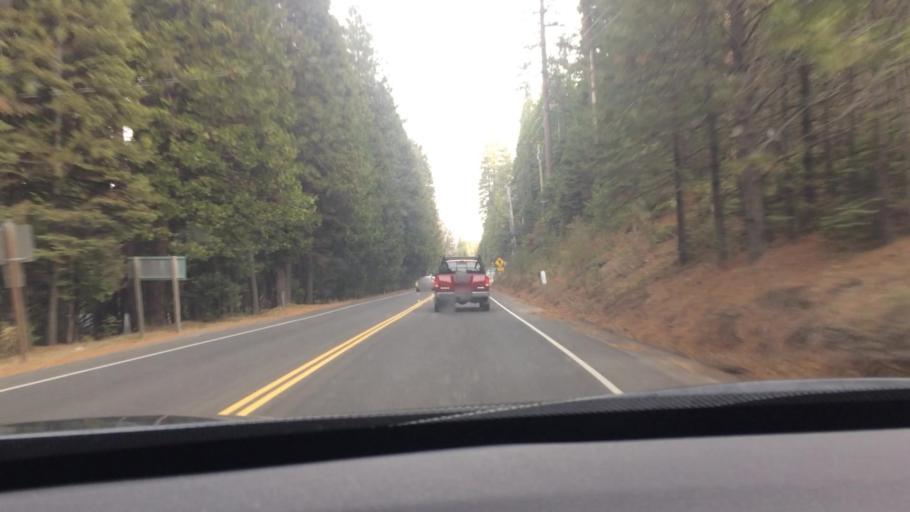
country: US
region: California
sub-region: Calaveras County
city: Arnold
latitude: 38.2515
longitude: -120.3572
